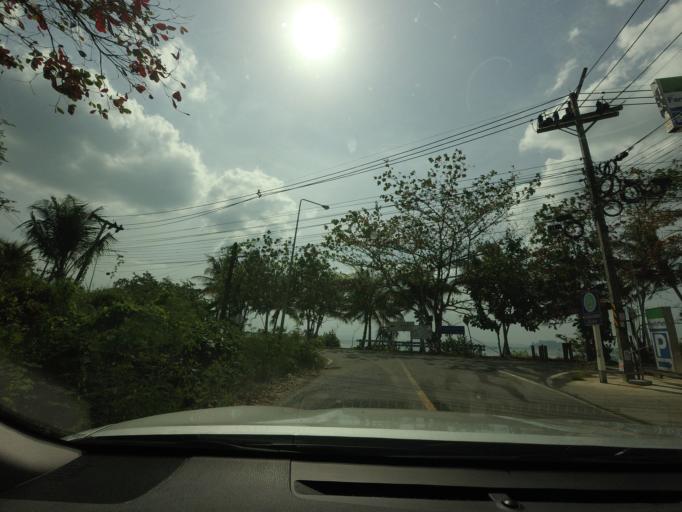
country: TH
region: Phangnga
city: Ban Ao Nang
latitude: 8.0722
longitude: 98.7451
